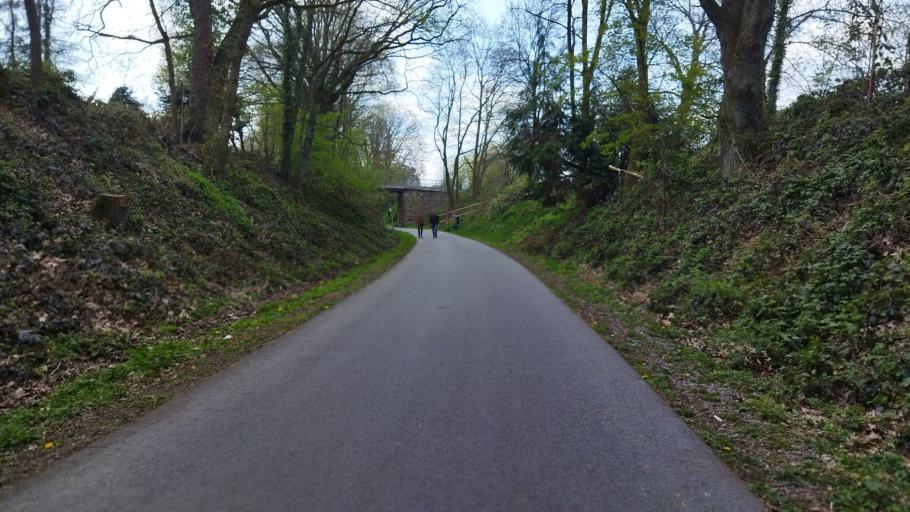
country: DE
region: North Rhine-Westphalia
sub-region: Regierungsbezirk Dusseldorf
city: Heiligenhaus
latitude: 51.3450
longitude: 6.9252
